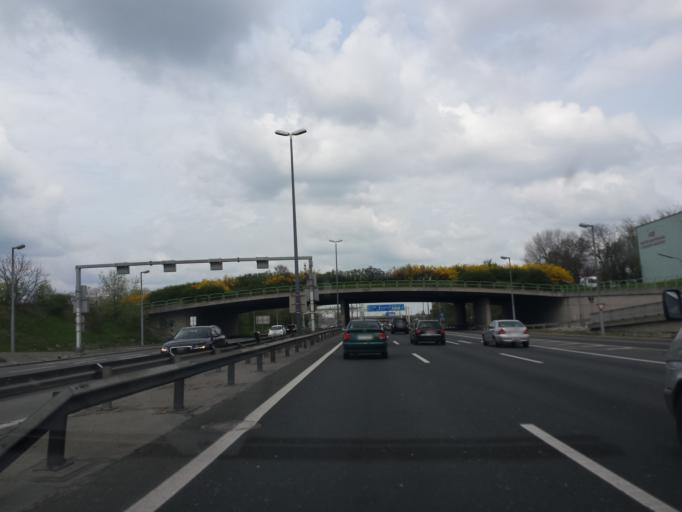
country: AT
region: Vienna
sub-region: Wien Stadt
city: Vienna
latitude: 48.2353
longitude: 16.4055
